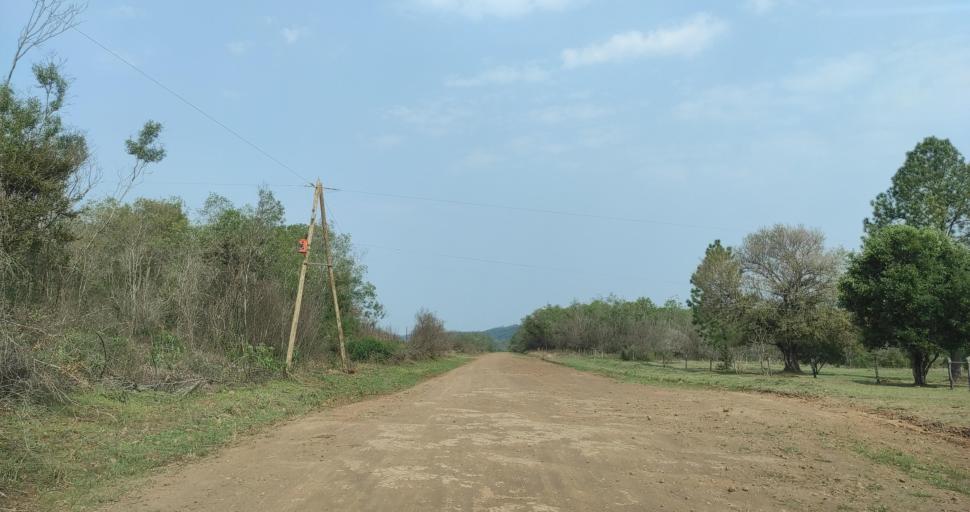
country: AR
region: Misiones
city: Cerro Cora
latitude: -27.5866
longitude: -55.5807
